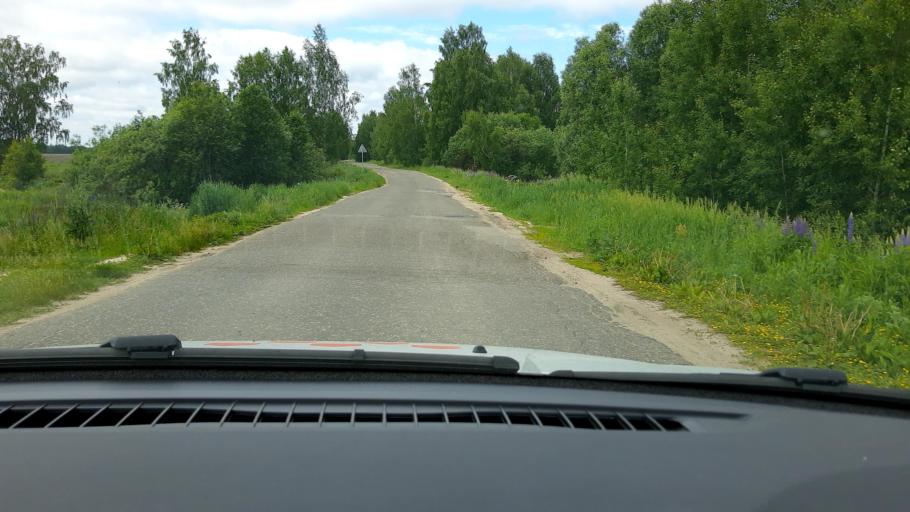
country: RU
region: Nizjnij Novgorod
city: Sitniki
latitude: 56.5261
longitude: 44.1027
